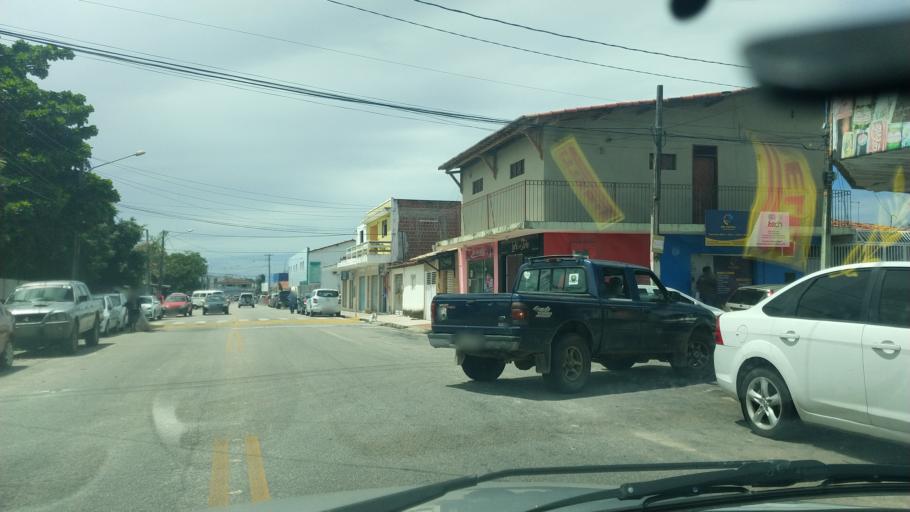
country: BR
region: Rio Grande do Norte
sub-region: Natal
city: Natal
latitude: -5.8256
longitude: -35.2366
